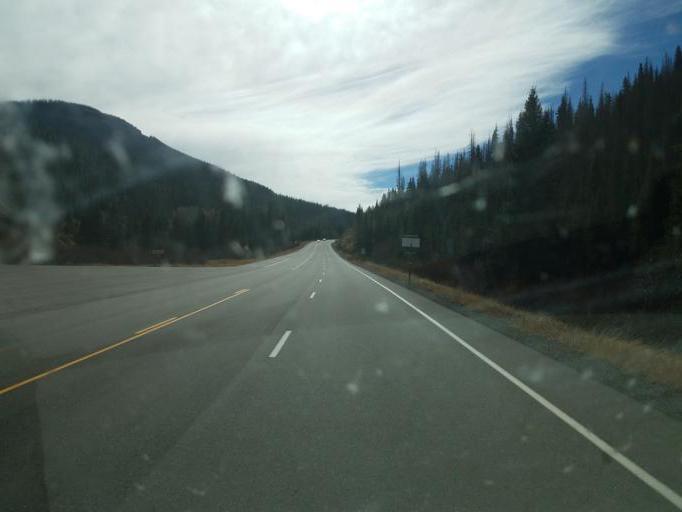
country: US
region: Colorado
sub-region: Archuleta County
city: Pagosa Springs
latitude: 37.5284
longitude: -106.7707
